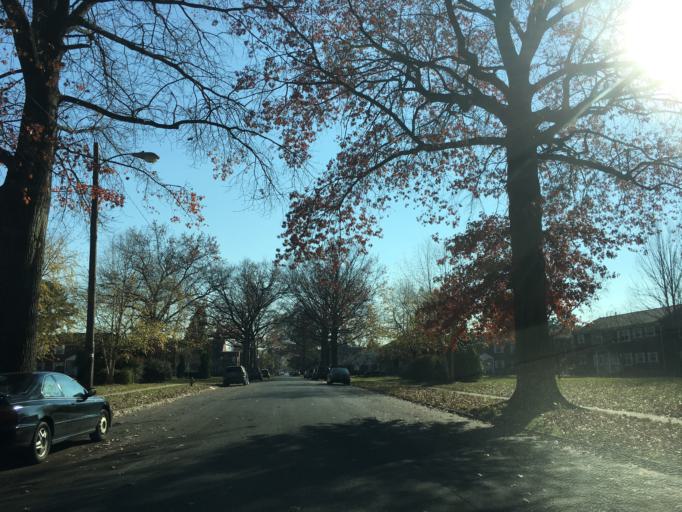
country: US
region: Pennsylvania
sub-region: Cumberland County
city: West Fairview
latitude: 40.2865
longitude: -76.9008
